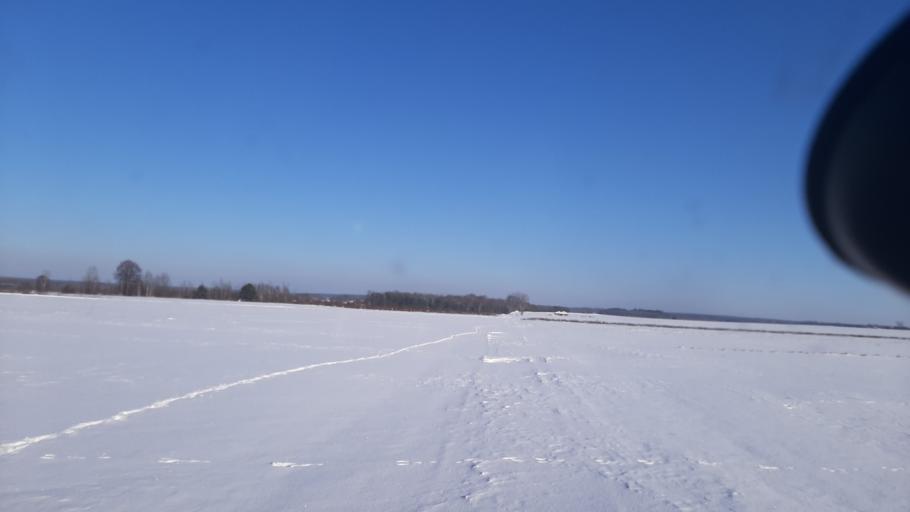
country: PL
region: Lublin Voivodeship
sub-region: Powiat lubelski
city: Jastkow
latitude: 51.3736
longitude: 22.4399
